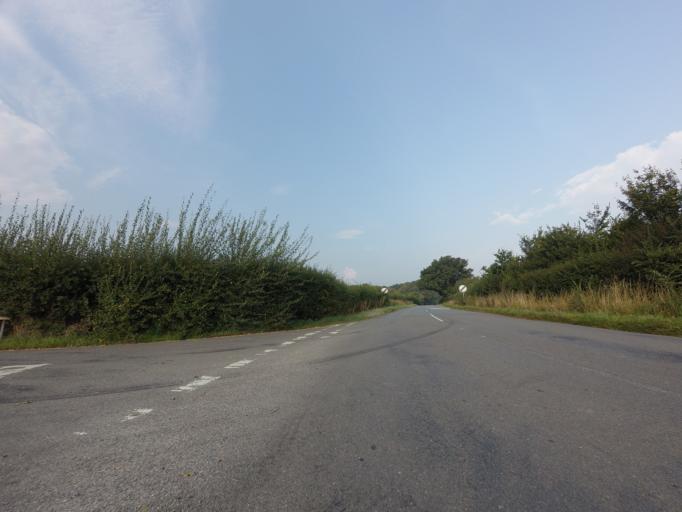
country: GB
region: England
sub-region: Kent
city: Ashford
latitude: 51.1071
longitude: 0.8118
